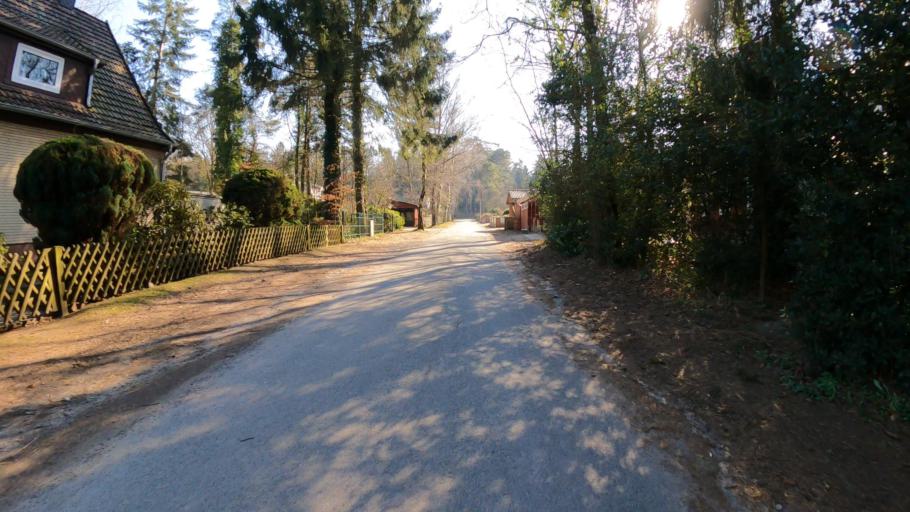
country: DE
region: Lower Saxony
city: Buchholz in der Nordheide
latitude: 53.3098
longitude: 9.8469
